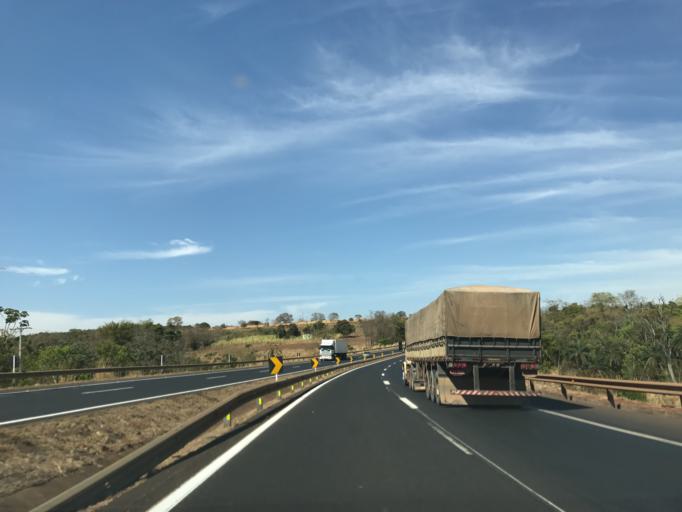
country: BR
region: Minas Gerais
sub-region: Monte Alegre De Minas
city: Monte Alegre de Minas
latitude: -18.8294
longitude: -49.0886
